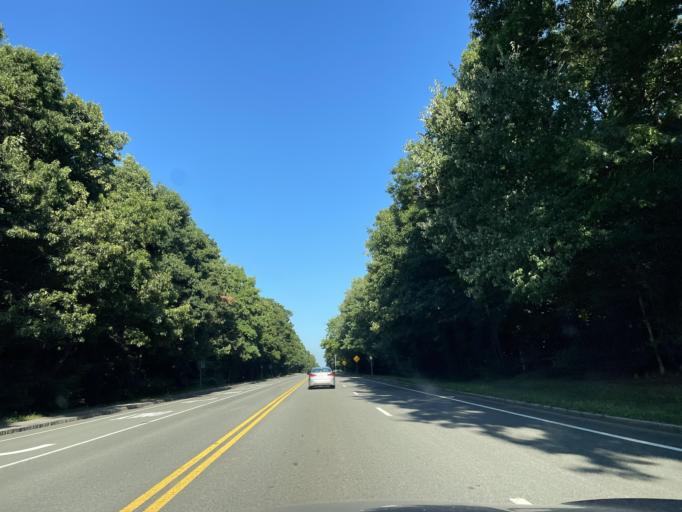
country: US
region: Massachusetts
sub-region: Bristol County
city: Easton
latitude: 42.0277
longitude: -71.1734
